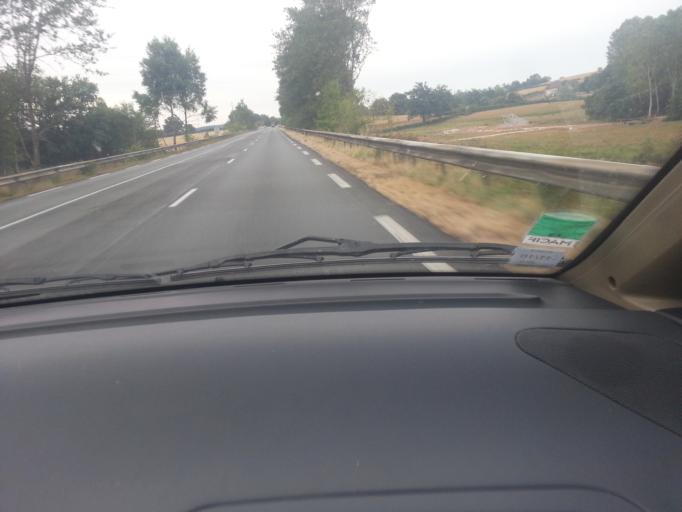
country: FR
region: Bourgogne
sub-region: Departement de Saone-et-Loire
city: Saint-Eusebe
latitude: 46.7172
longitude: 4.4379
